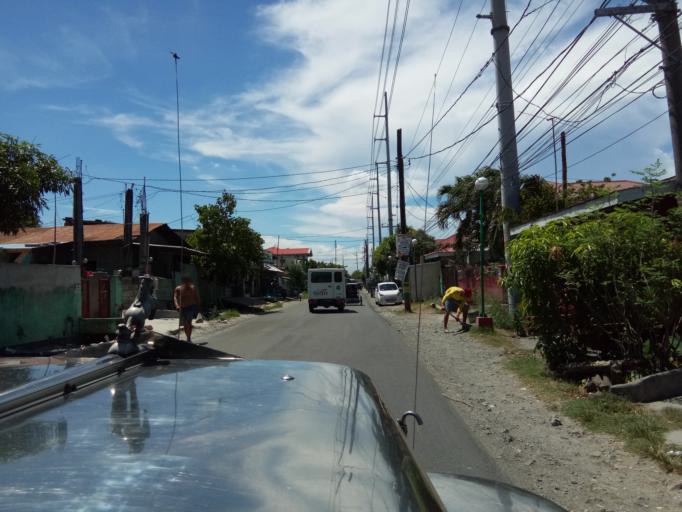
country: PH
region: Calabarzon
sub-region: Province of Cavite
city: Pasong Kawayan Primero
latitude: 14.3633
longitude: 120.8949
